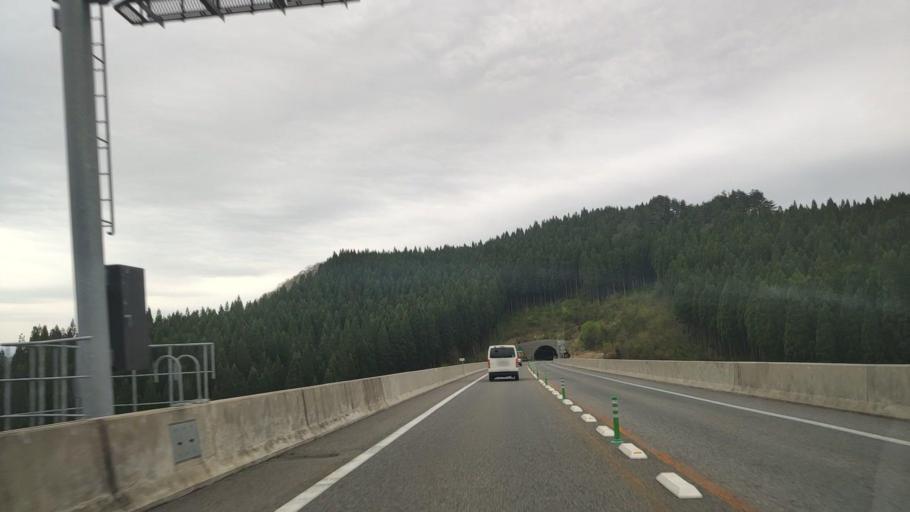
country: JP
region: Akita
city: Odate
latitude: 40.3267
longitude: 140.6045
